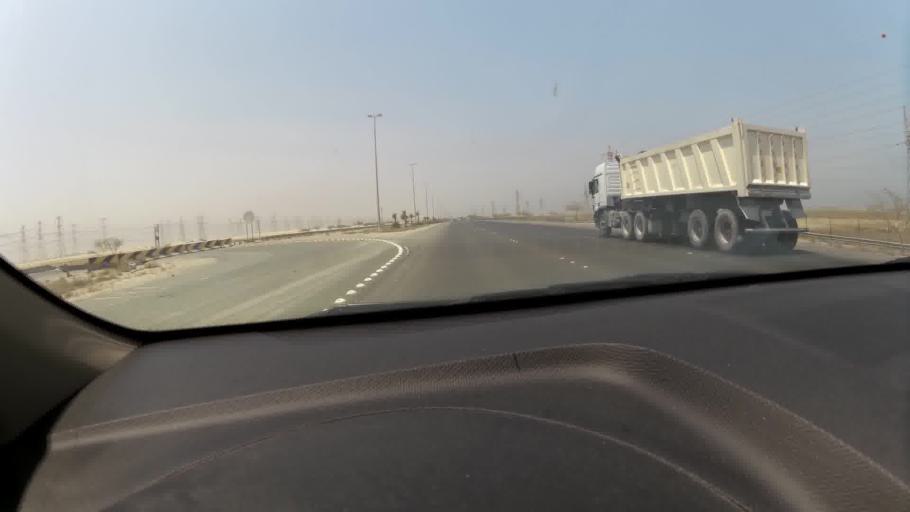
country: KW
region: Al Ahmadi
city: Al Fahahil
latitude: 28.8313
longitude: 48.2546
